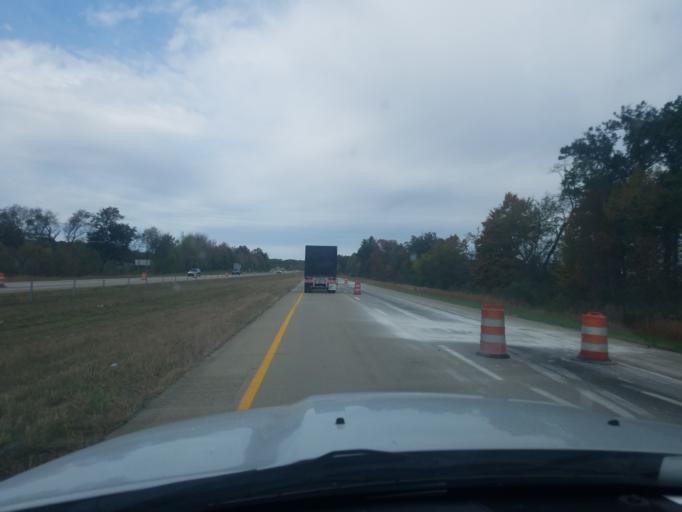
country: US
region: Indiana
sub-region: Gibson County
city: Haubstadt
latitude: 38.1548
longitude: -87.4725
